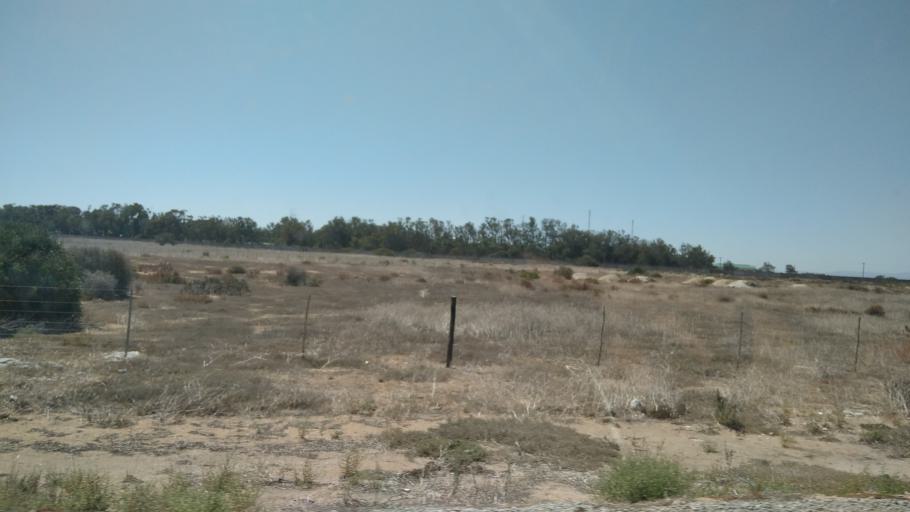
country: ZA
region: Western Cape
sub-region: West Coast District Municipality
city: Vredenburg
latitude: -32.9863
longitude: 18.1459
